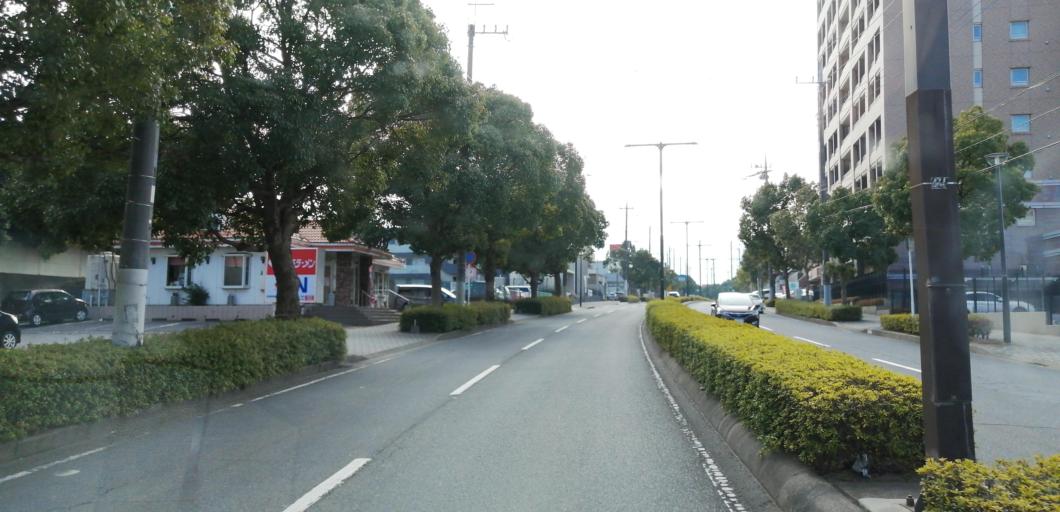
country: JP
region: Chiba
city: Narita
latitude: 35.7576
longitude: 140.2982
